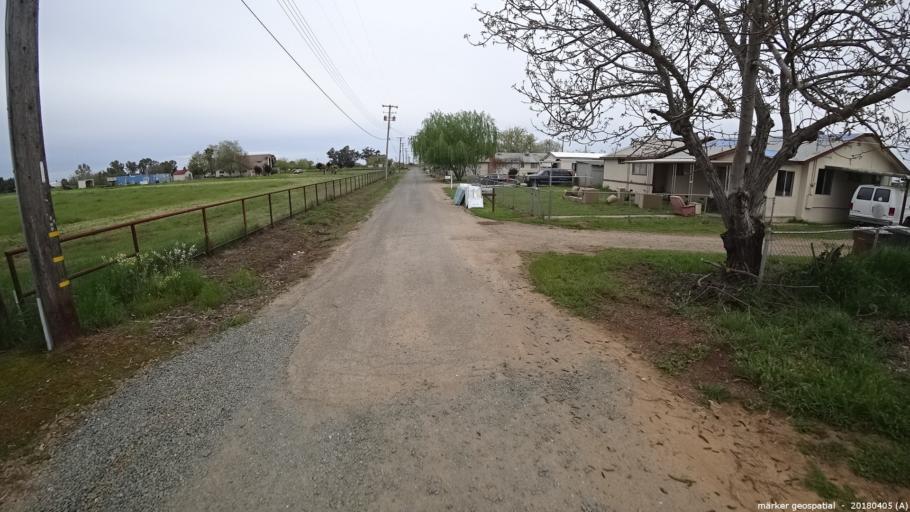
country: US
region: California
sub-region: Sacramento County
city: Herald
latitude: 38.2995
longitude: -121.2218
